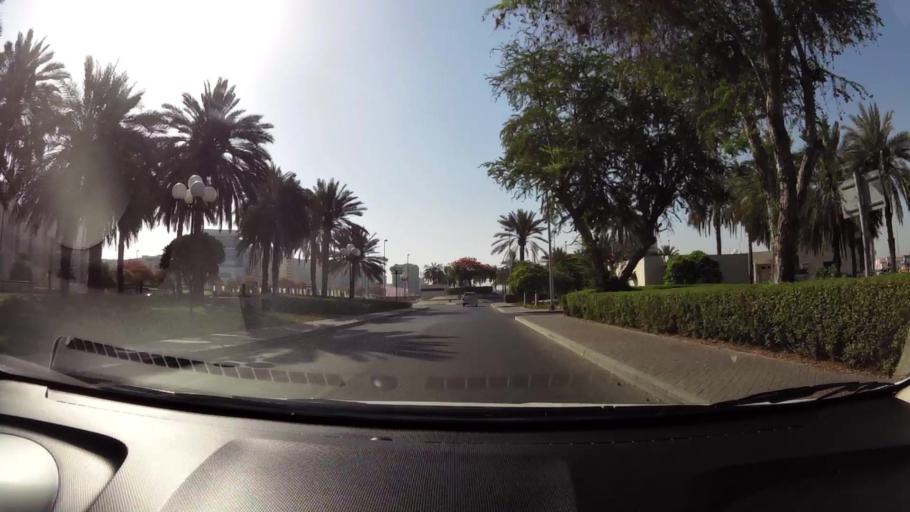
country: AE
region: Ash Shariqah
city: Sharjah
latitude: 25.2566
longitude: 55.3213
